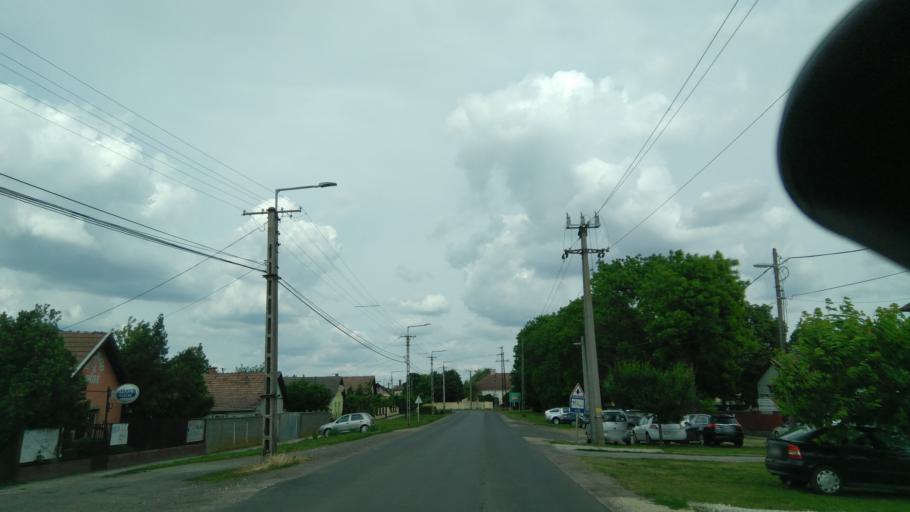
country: HU
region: Bekes
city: Mezohegyes
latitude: 46.3204
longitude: 20.8146
